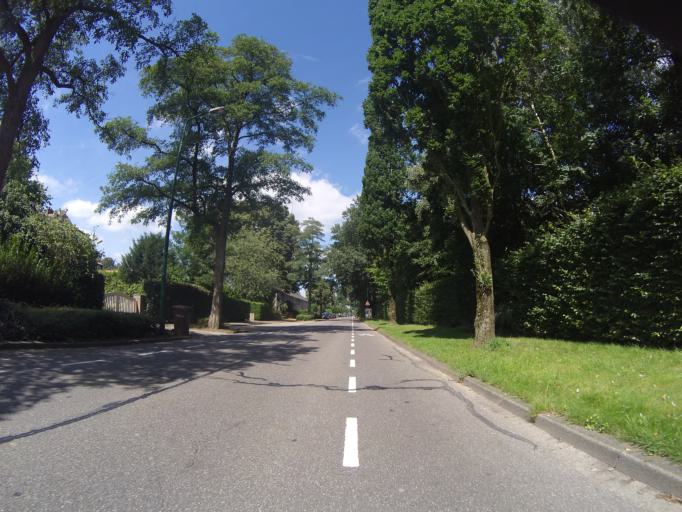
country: NL
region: Utrecht
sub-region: Gemeente Soest
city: Soest
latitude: 52.1185
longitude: 5.2872
